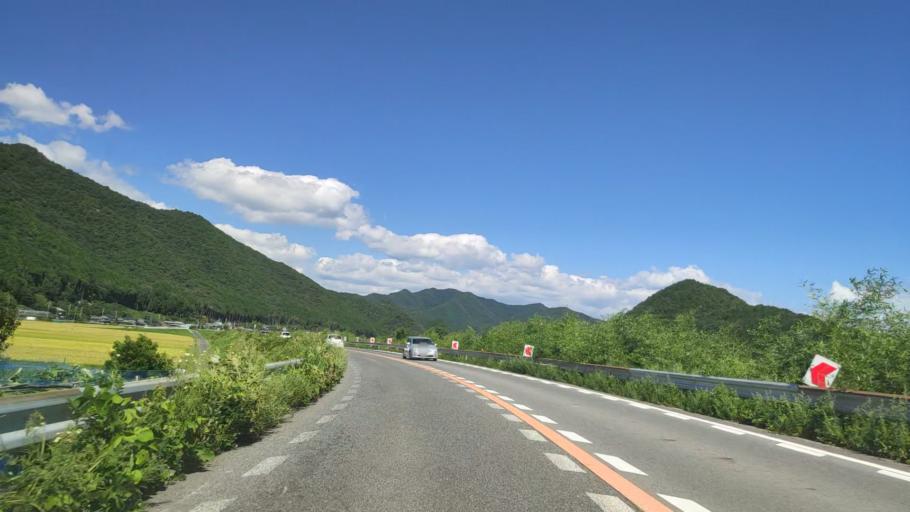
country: JP
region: Hyogo
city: Nishiwaki
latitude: 35.0262
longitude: 134.9845
